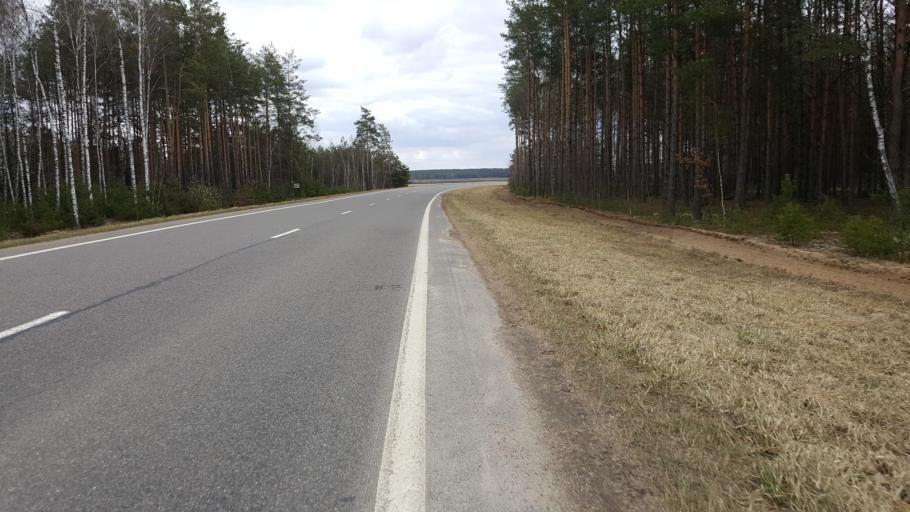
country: BY
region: Brest
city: Kamyanyuki
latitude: 52.5080
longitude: 23.7424
